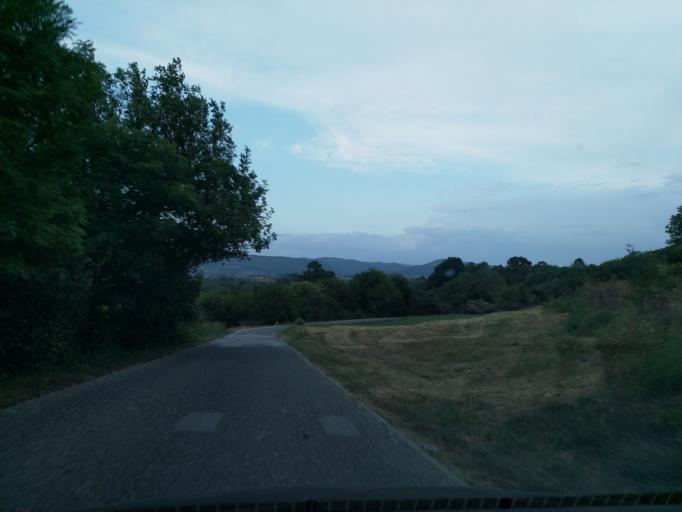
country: RS
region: Central Serbia
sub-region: Pomoravski Okrug
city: Paracin
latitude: 43.8559
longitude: 21.5301
